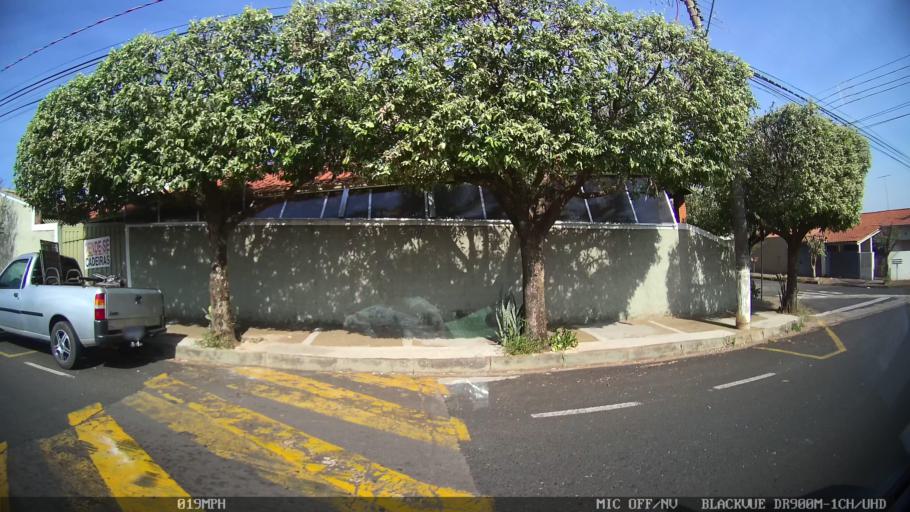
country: BR
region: Sao Paulo
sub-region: Sao Jose Do Rio Preto
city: Sao Jose do Rio Preto
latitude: -20.7979
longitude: -49.4227
